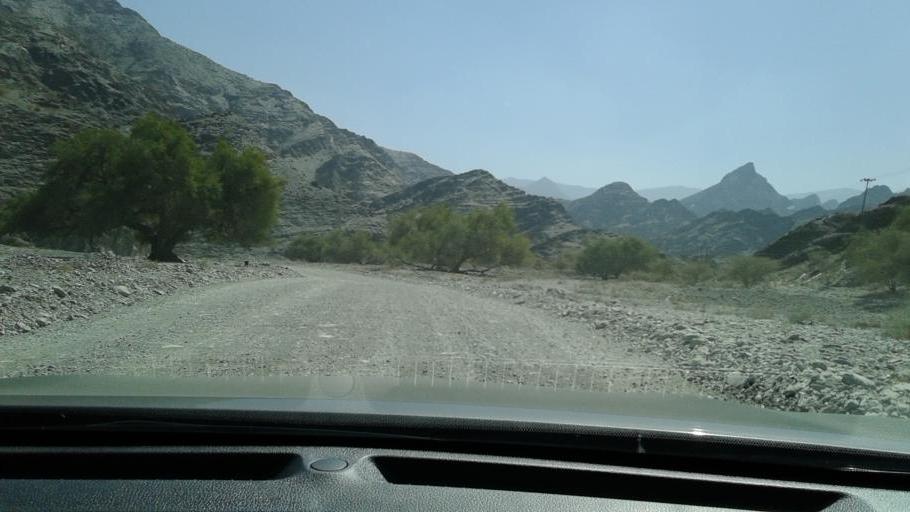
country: OM
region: Al Batinah
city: Bayt al `Awabi
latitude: 23.2661
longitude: 57.4468
